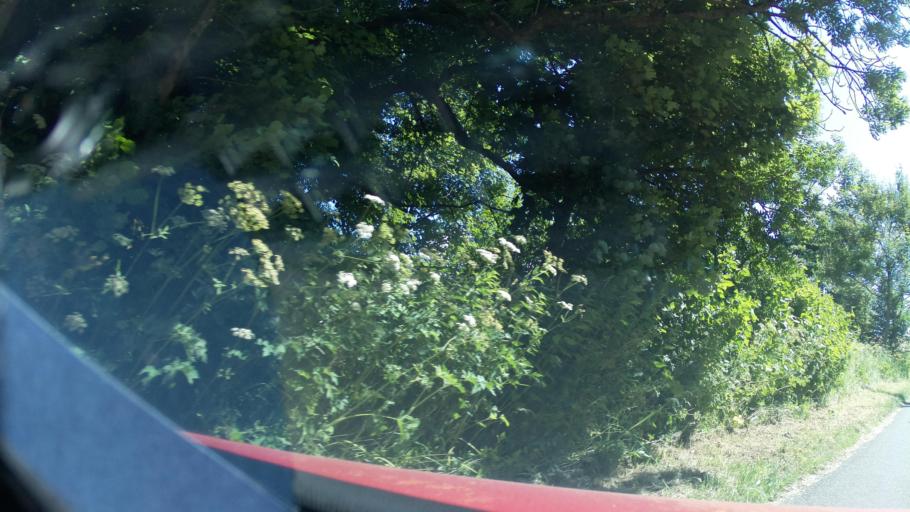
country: GB
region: England
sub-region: Derbyshire
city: Buxton
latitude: 53.2870
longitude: -1.8614
